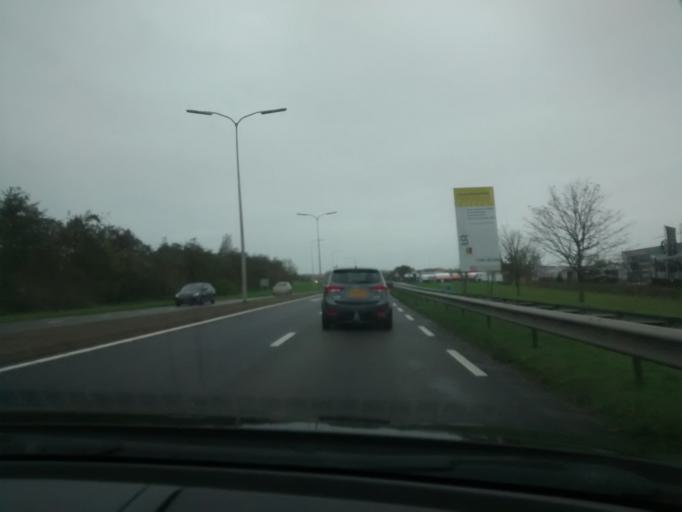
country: NL
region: South Holland
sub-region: Gemeente Katwijk
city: Rijnsburg
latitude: 52.1718
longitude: 4.4407
